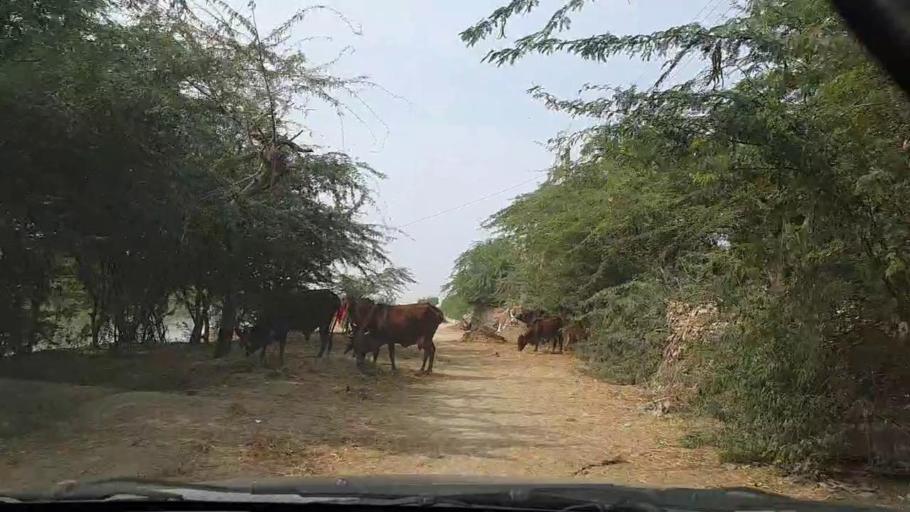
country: PK
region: Sindh
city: Thatta
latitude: 24.5715
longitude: 67.8551
